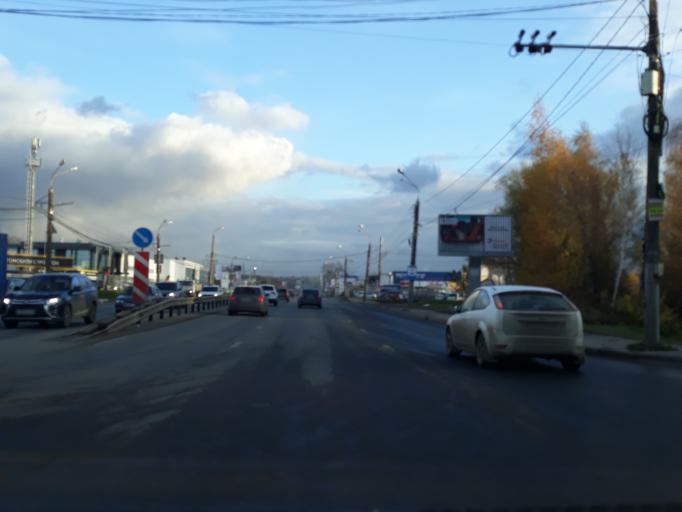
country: RU
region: Nizjnij Novgorod
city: Nizhniy Novgorod
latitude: 56.3024
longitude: 43.9201
